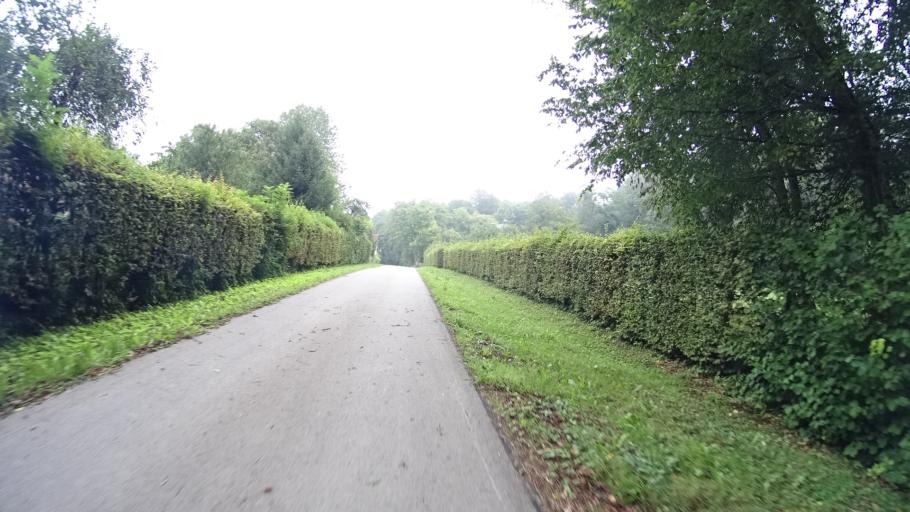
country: DE
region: Bavaria
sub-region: Upper Bavaria
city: Stammham
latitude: 48.8736
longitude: 11.5109
